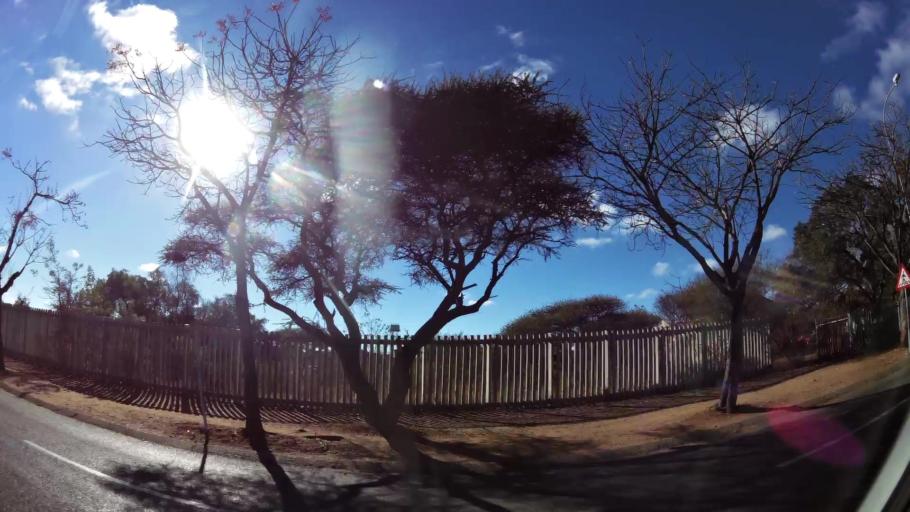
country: ZA
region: Limpopo
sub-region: Capricorn District Municipality
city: Polokwane
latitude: -23.8937
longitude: 29.4563
